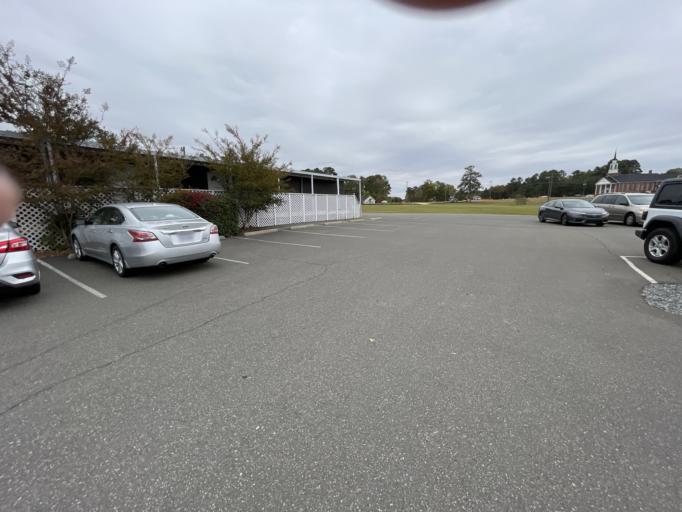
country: US
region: North Carolina
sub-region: Durham County
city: Durham
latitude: 35.9722
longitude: -78.8488
